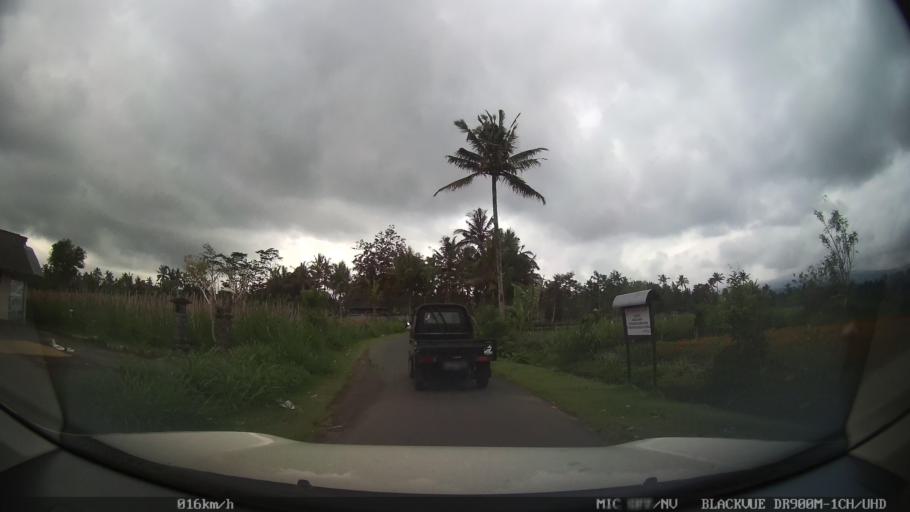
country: ID
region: Bali
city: Banjar Wangsian
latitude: -8.4419
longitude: 115.4254
